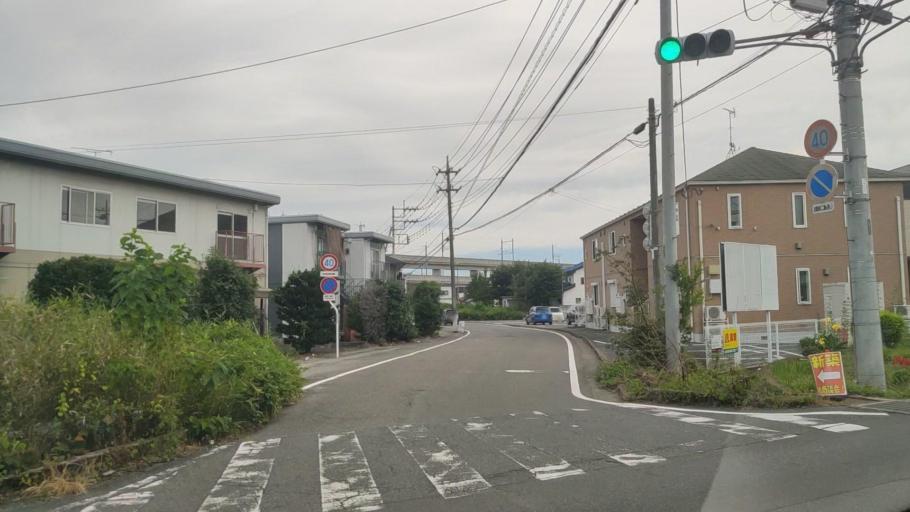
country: JP
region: Gunma
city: Takasaki
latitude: 36.3583
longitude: 138.9945
